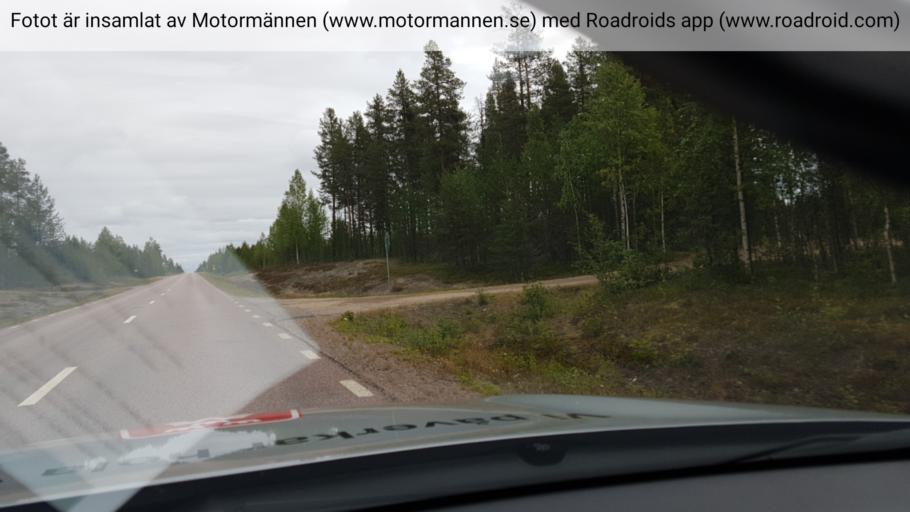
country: SE
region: Norrbotten
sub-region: Overkalix Kommun
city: OEverkalix
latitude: 67.0818
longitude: 22.5429
